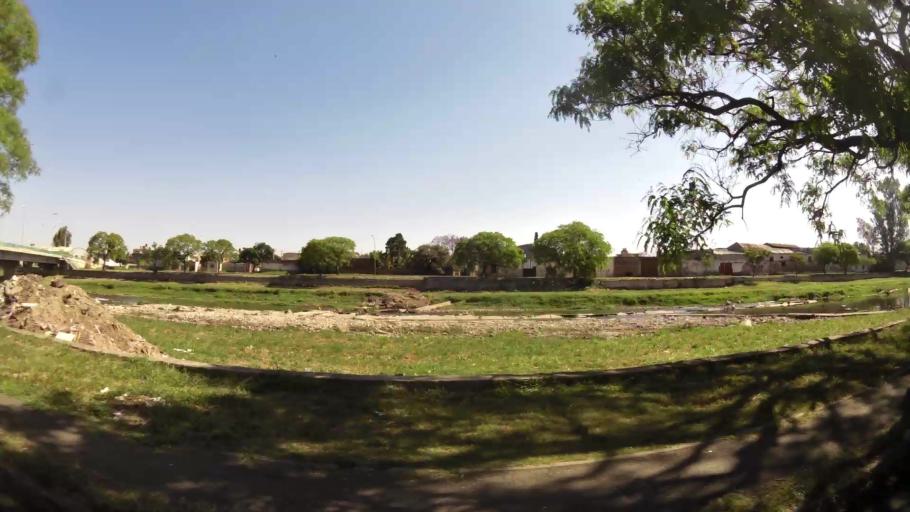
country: AR
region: Cordoba
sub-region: Departamento de Capital
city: Cordoba
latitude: -31.4175
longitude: -64.1519
